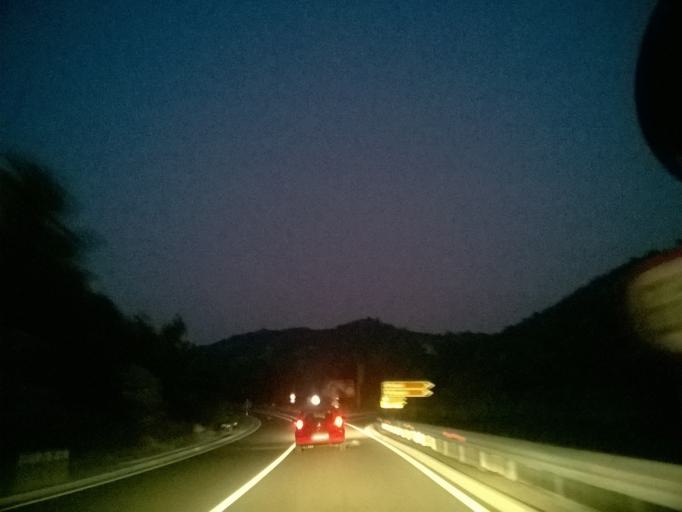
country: ME
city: Mojanovici
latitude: 42.3831
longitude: 19.1012
